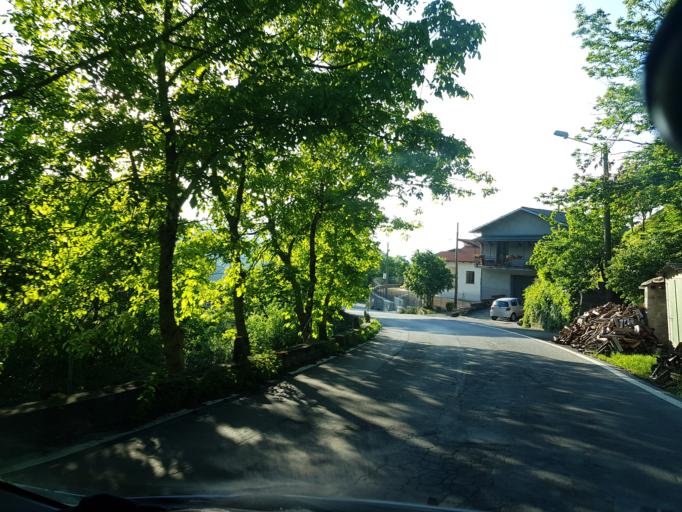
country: IT
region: Tuscany
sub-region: Provincia di Lucca
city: Minucciano
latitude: 44.1678
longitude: 10.2098
